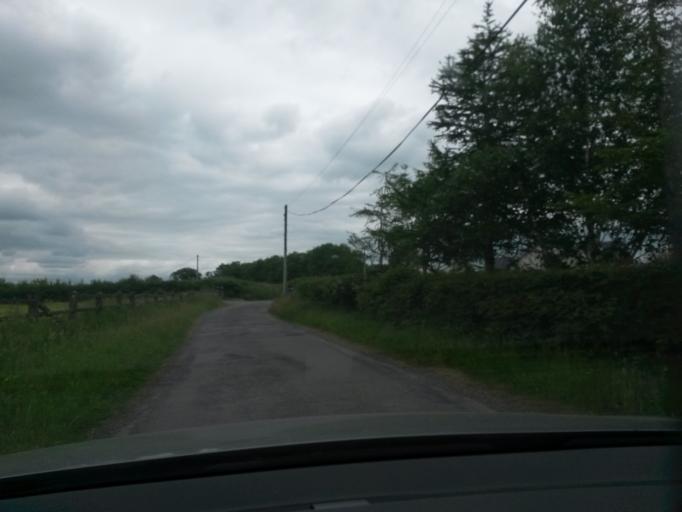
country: IE
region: Munster
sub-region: An Clar
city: Ennis
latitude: 52.9143
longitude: -9.0520
